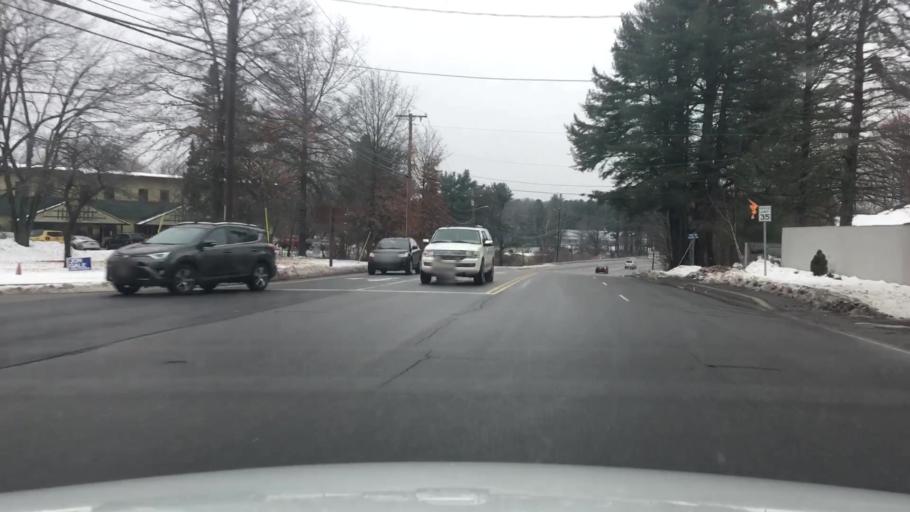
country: US
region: Maine
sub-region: Cumberland County
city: South Portland Gardens
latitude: 43.6112
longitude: -70.3130
